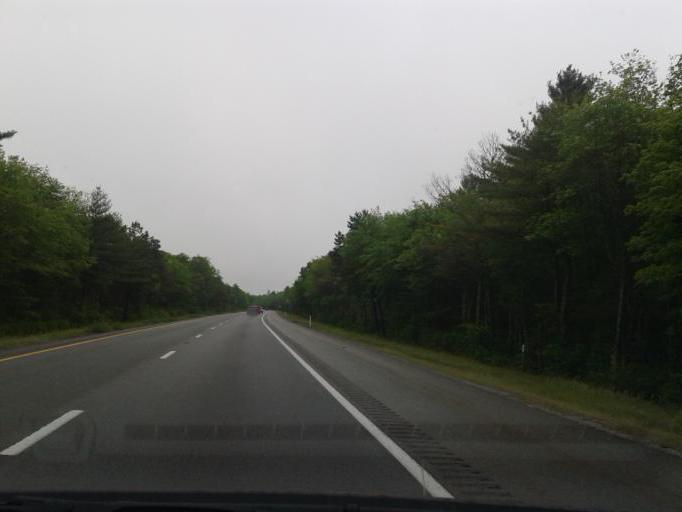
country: US
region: Massachusetts
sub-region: Plymouth County
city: Marion Center
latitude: 41.7130
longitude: -70.7894
